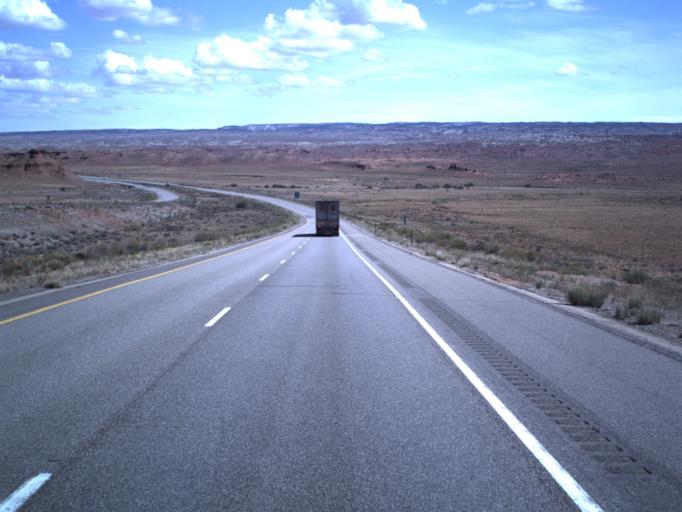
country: US
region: Utah
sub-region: Emery County
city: Ferron
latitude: 38.8389
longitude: -111.0833
